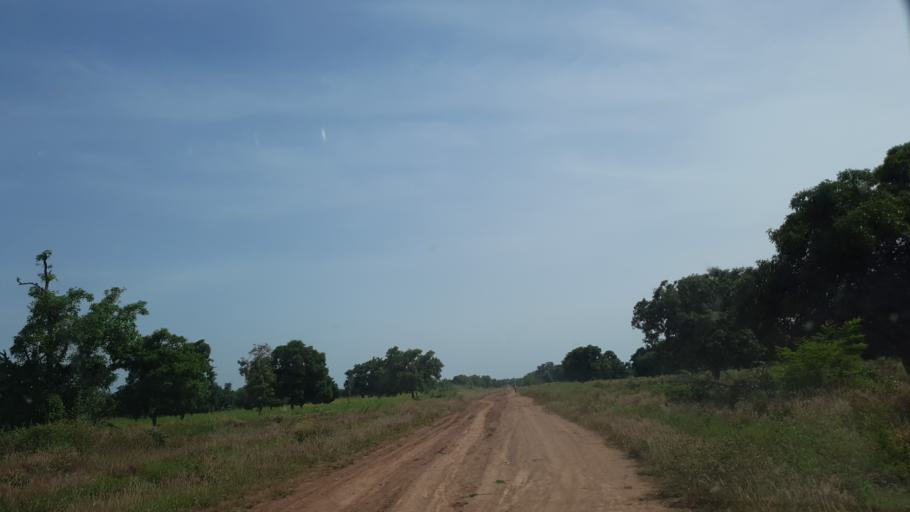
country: ML
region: Koulikoro
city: Dioila
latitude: 12.4196
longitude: -6.2311
